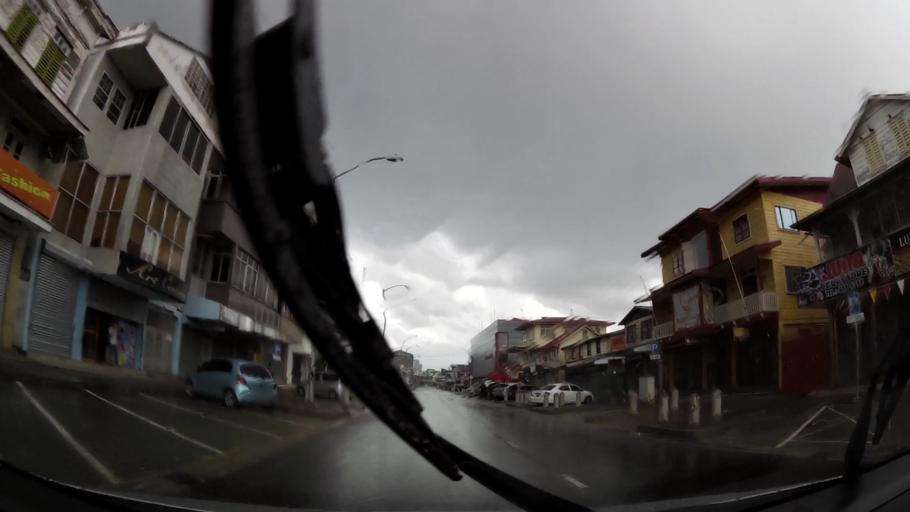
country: SR
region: Paramaribo
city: Paramaribo
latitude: 5.8252
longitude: -55.1594
